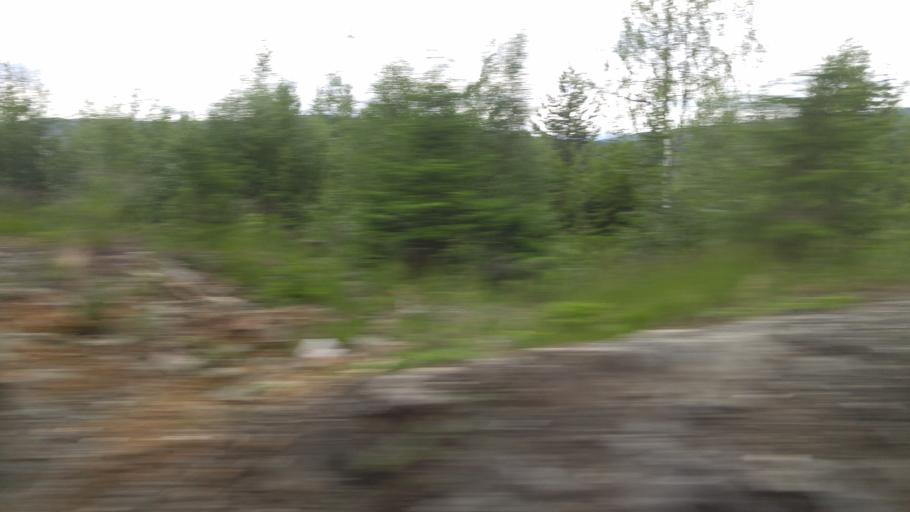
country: NO
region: Nord-Trondelag
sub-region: Meraker
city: Meraker
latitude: 63.4015
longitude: 11.8258
